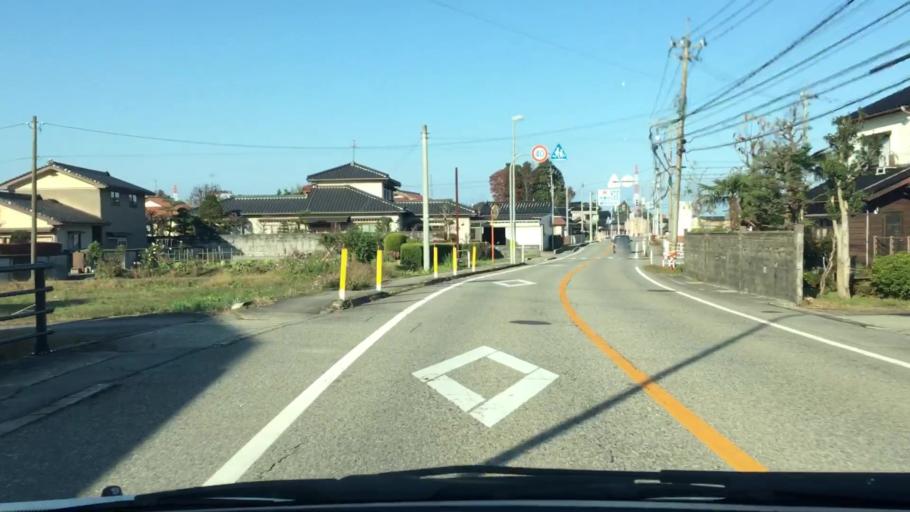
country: JP
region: Toyama
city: Kamiichi
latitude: 36.7053
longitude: 137.3107
